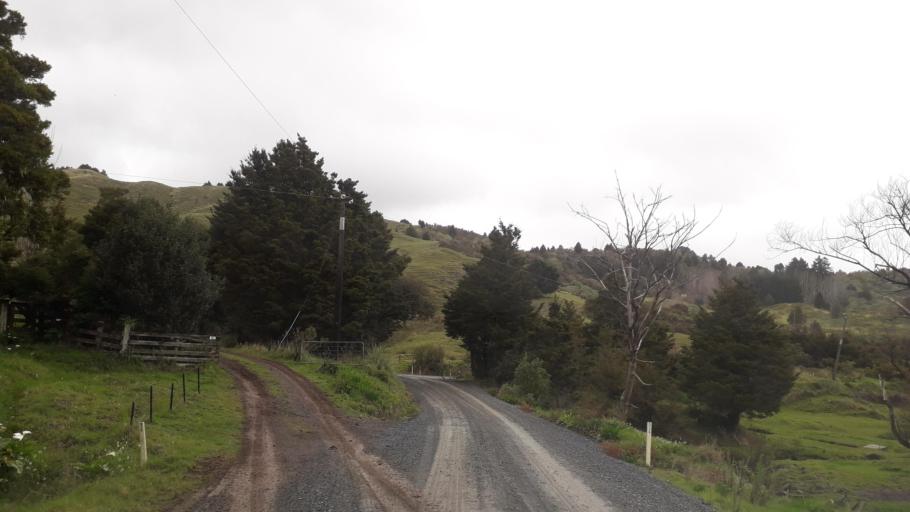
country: NZ
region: Northland
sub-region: Far North District
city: Kerikeri
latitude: -35.1316
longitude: 173.7390
